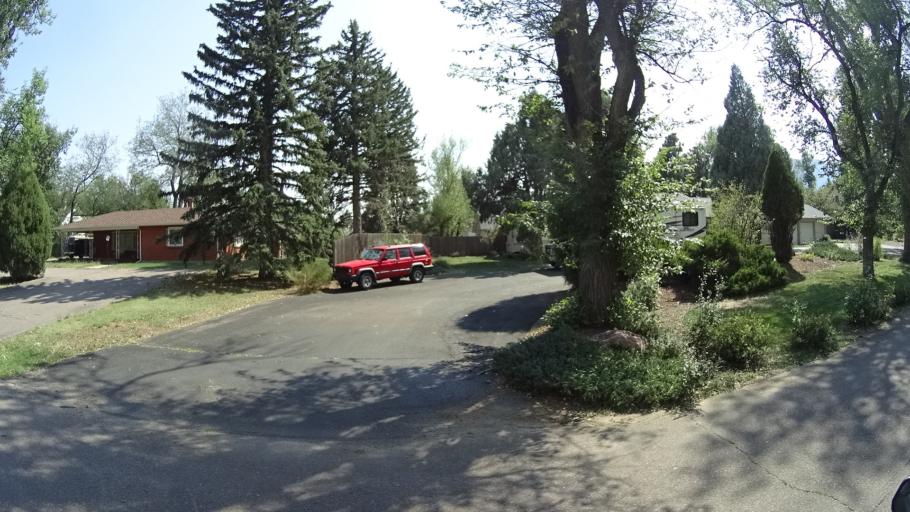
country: US
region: Colorado
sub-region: El Paso County
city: Colorado Springs
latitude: 38.7990
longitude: -104.8343
